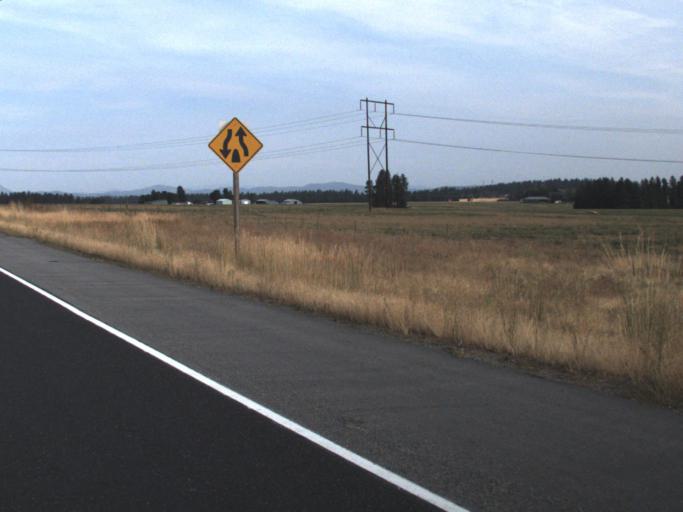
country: US
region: Washington
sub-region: Spokane County
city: Fairwood
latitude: 47.8480
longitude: -117.4218
